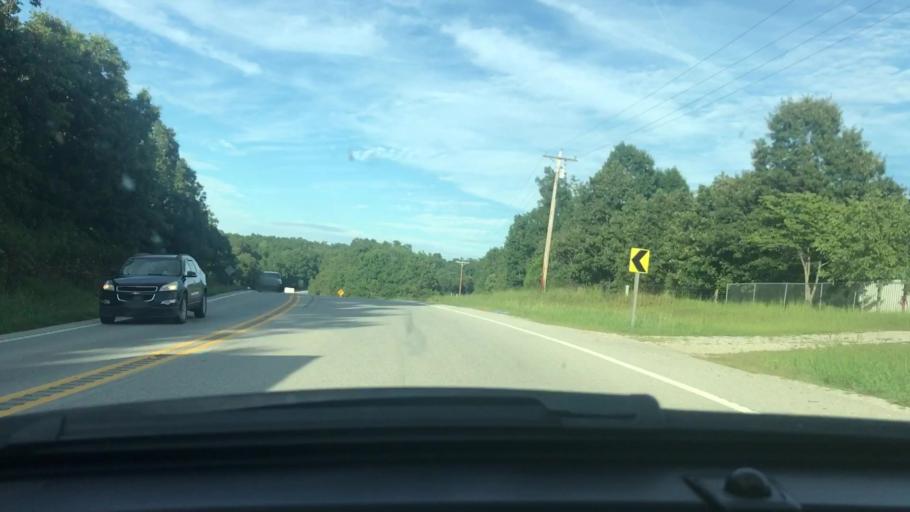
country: US
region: Arkansas
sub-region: Sharp County
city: Cherokee Village
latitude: 36.2742
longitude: -91.3178
